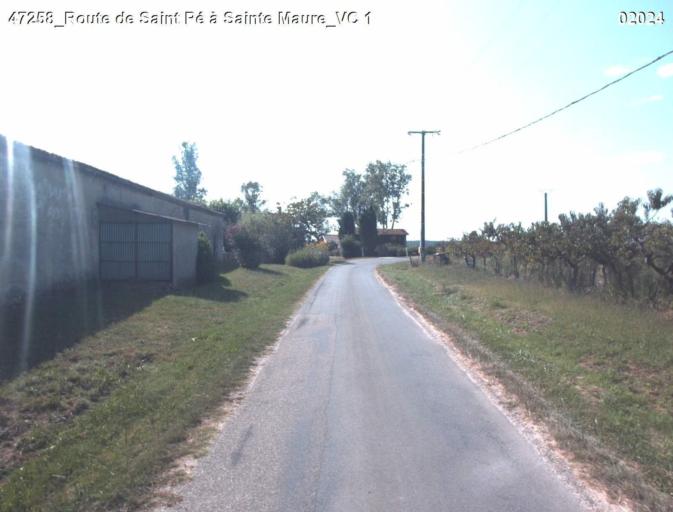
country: FR
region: Midi-Pyrenees
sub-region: Departement du Gers
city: Montreal
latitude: 44.0134
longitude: 0.1441
